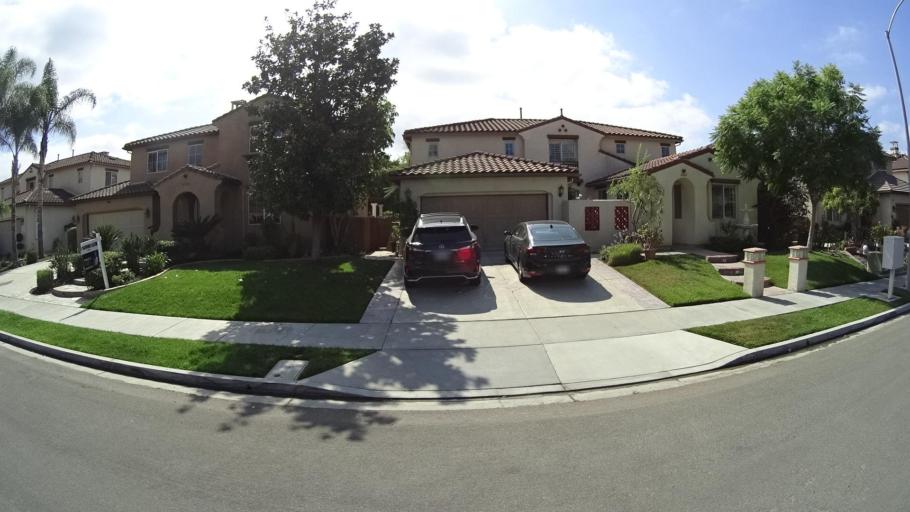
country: US
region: California
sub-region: San Diego County
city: Fairbanks Ranch
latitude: 33.0054
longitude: -117.1069
